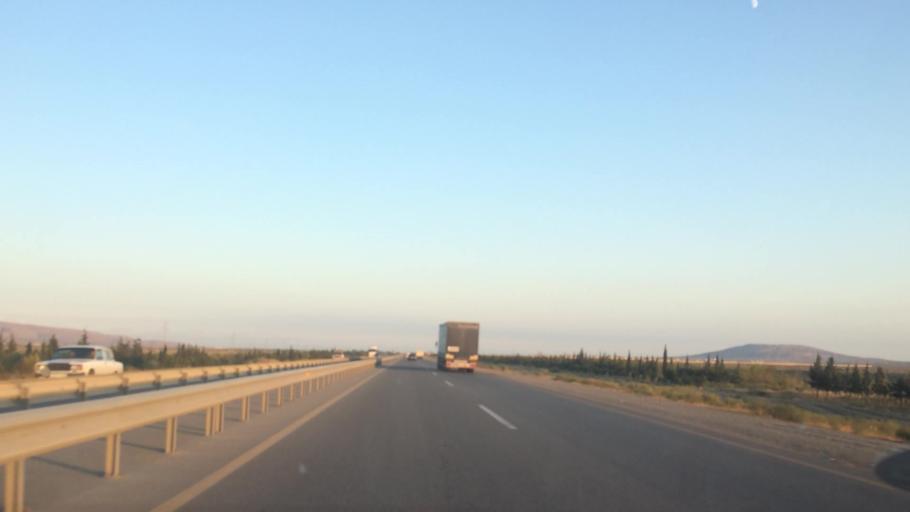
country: AZ
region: Baki
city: Qobustan
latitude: 39.9934
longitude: 49.1936
